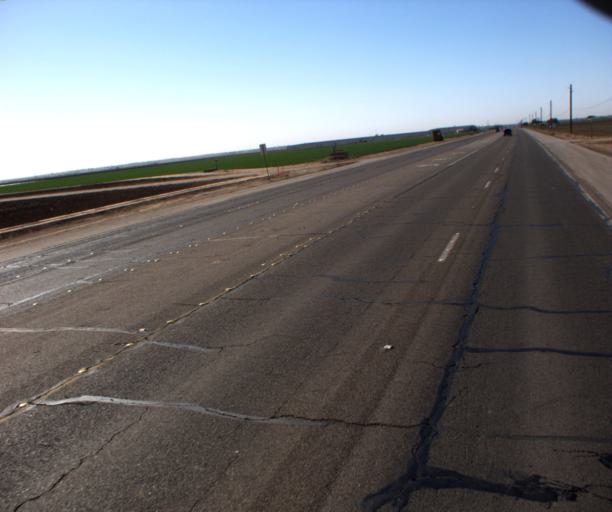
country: US
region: Arizona
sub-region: Yuma County
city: San Luis
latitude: 32.5388
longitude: -114.7870
